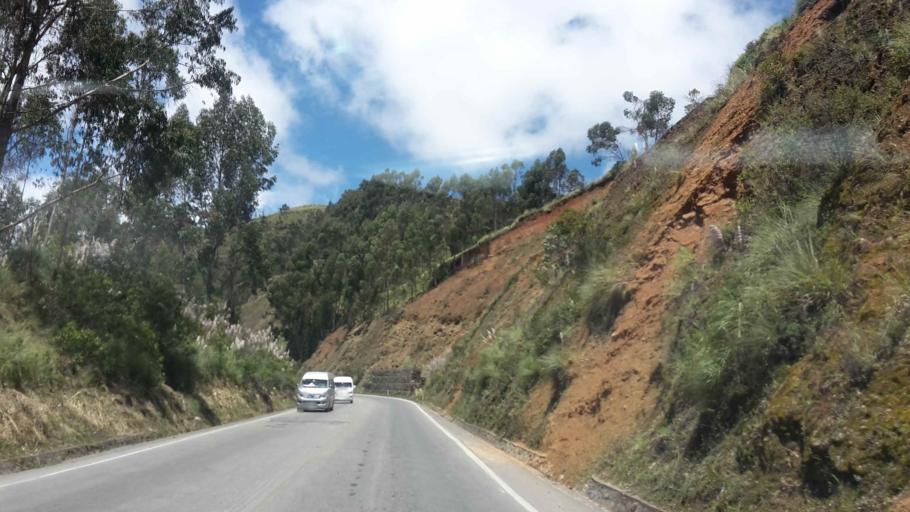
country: BO
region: Cochabamba
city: Colomi
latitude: -17.3170
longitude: -65.8690
